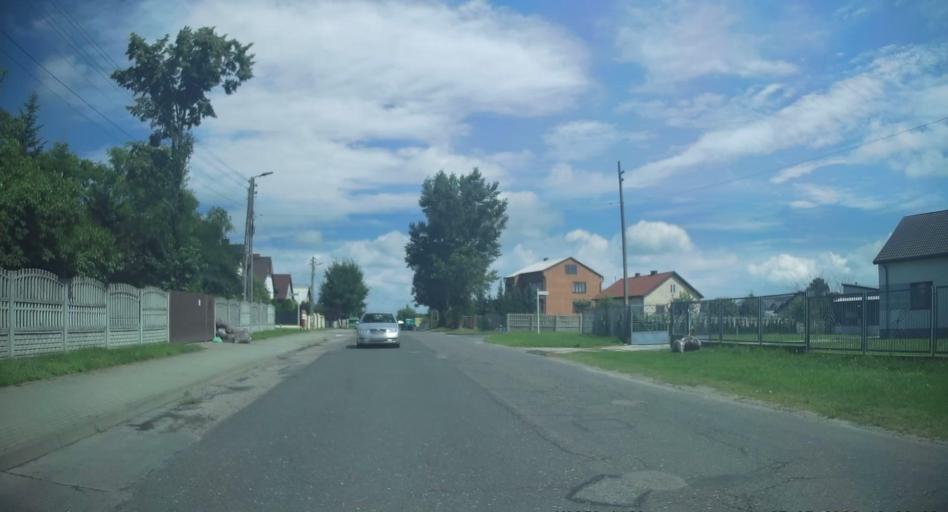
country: PL
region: Lodz Voivodeship
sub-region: Powiat rawski
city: Rawa Mazowiecka
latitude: 51.7497
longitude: 20.2398
